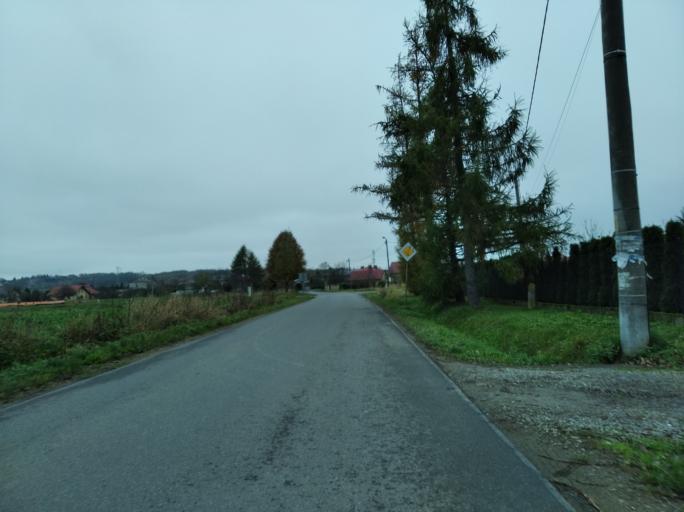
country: PL
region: Subcarpathian Voivodeship
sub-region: Powiat krosnienski
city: Odrzykon
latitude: 49.7249
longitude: 21.7632
